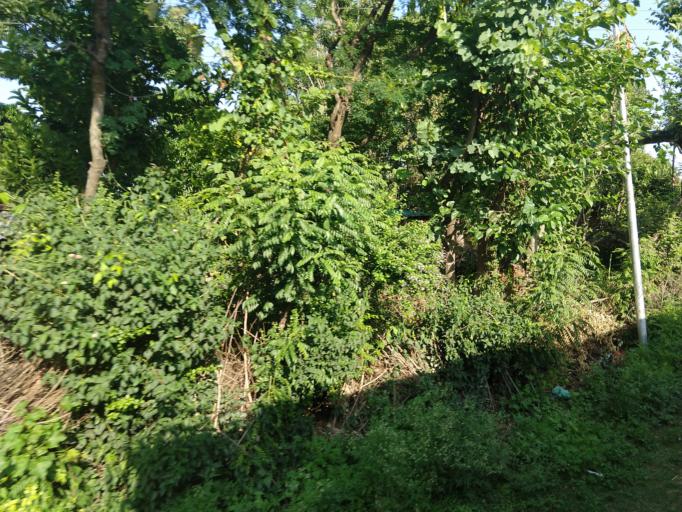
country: IN
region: Himachal Pradesh
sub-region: Chamba
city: Chowari
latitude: 32.3671
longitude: 75.9210
